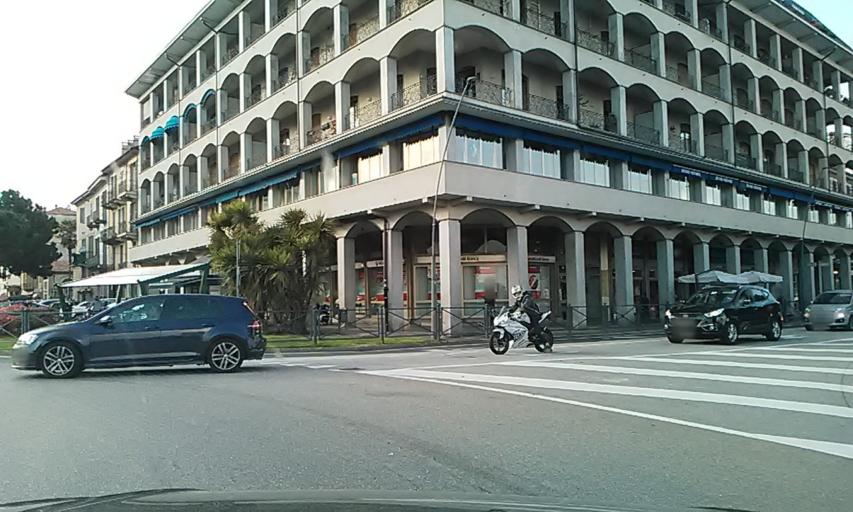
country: IT
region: Piedmont
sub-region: Provincia Verbano-Cusio-Ossola
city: Pallanza-Intra-Suna
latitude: 45.9343
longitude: 8.5731
